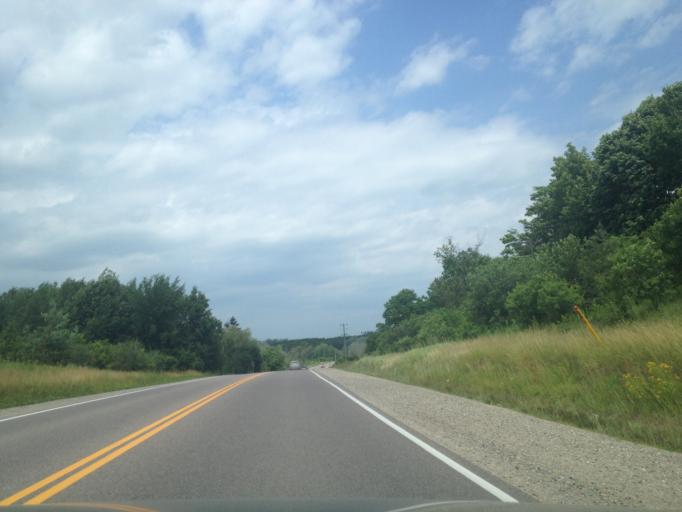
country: CA
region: Ontario
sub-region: Wellington County
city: Guelph
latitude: 43.5819
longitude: -80.2459
